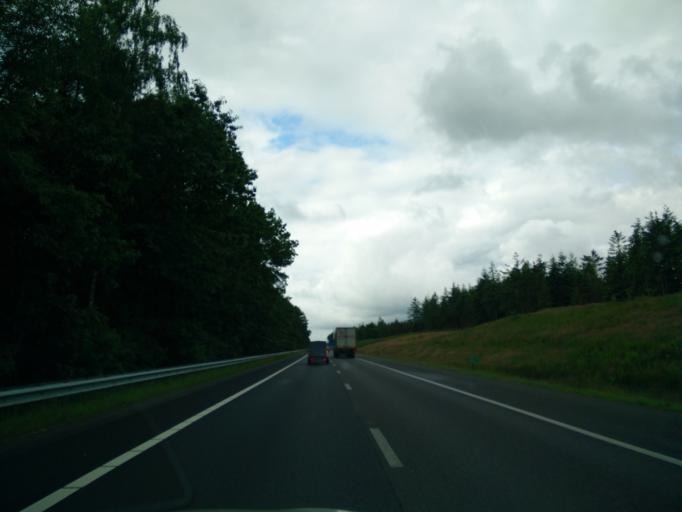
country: NL
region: Drenthe
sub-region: Gemeente Westerveld
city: Dwingeloo
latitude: 52.8308
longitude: 6.4749
